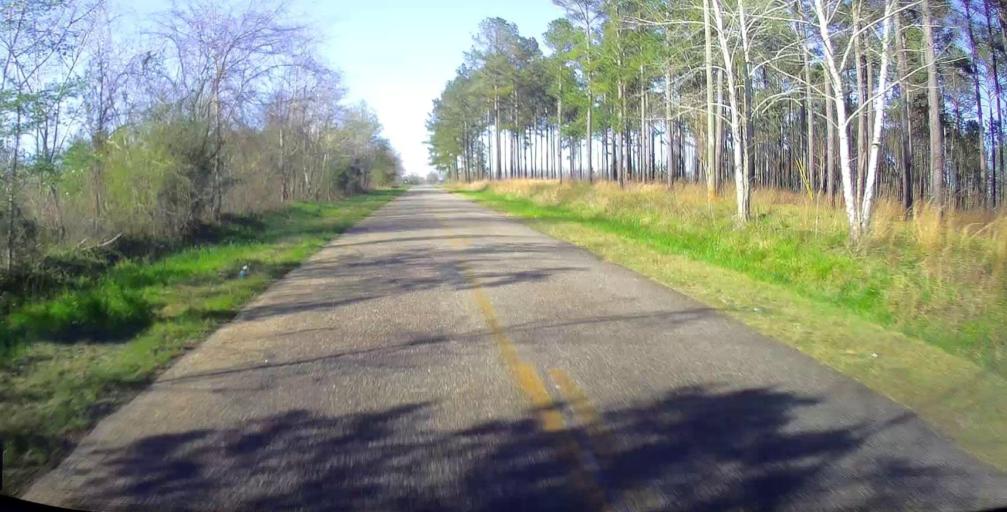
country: US
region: Georgia
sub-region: Macon County
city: Marshallville
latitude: 32.4796
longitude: -83.9522
